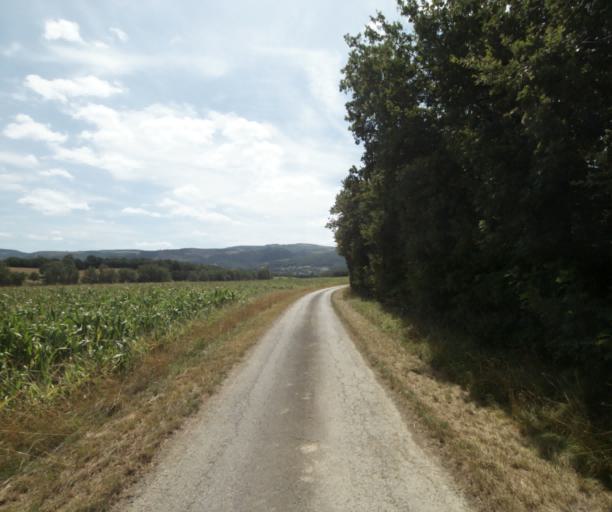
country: FR
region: Midi-Pyrenees
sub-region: Departement du Tarn
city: Dourgne
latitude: 43.4884
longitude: 2.1001
